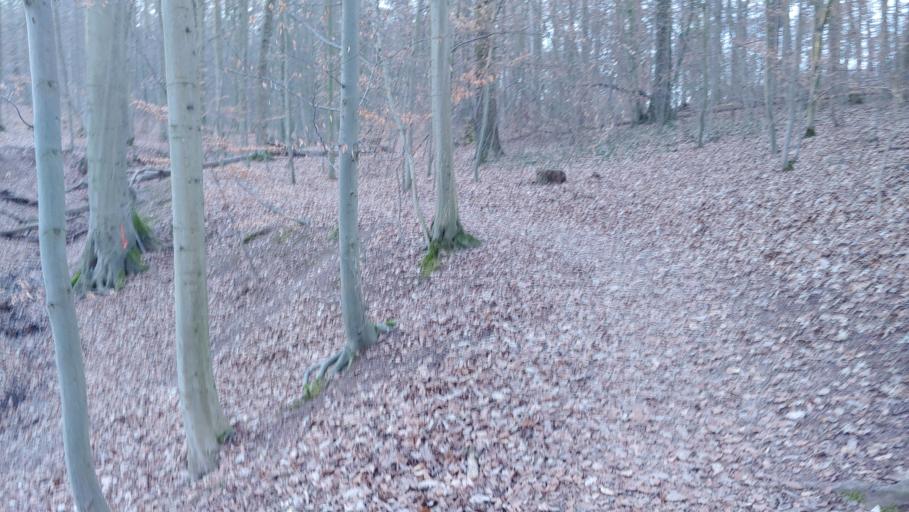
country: DE
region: Hesse
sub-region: Regierungsbezirk Kassel
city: Vellmar
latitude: 51.3274
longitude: 9.4230
